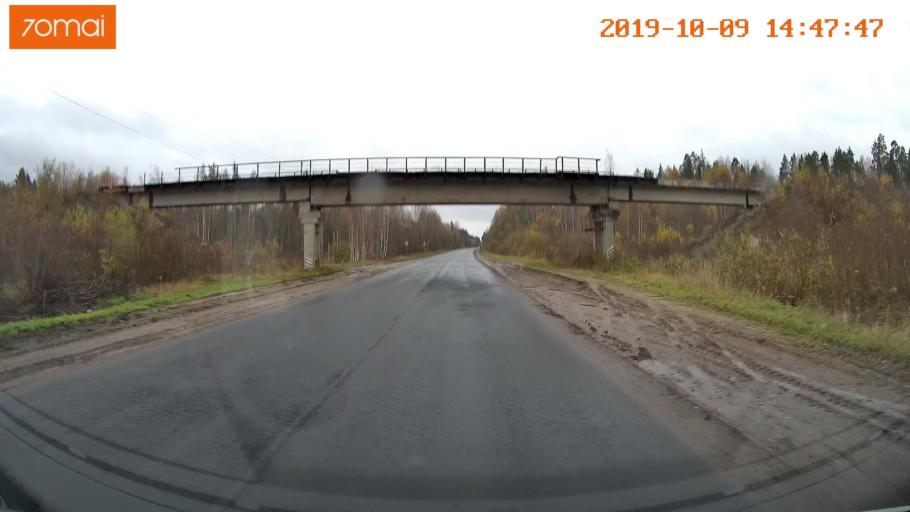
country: RU
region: Kostroma
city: Chistyye Bory
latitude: 58.4139
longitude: 41.5721
